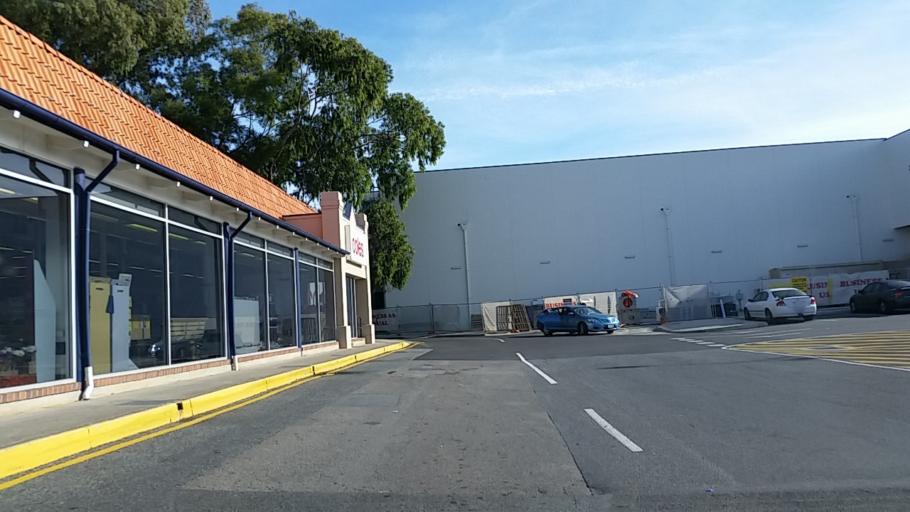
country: AU
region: South Australia
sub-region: Salisbury
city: Salisbury
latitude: -34.7607
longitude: 138.6480
